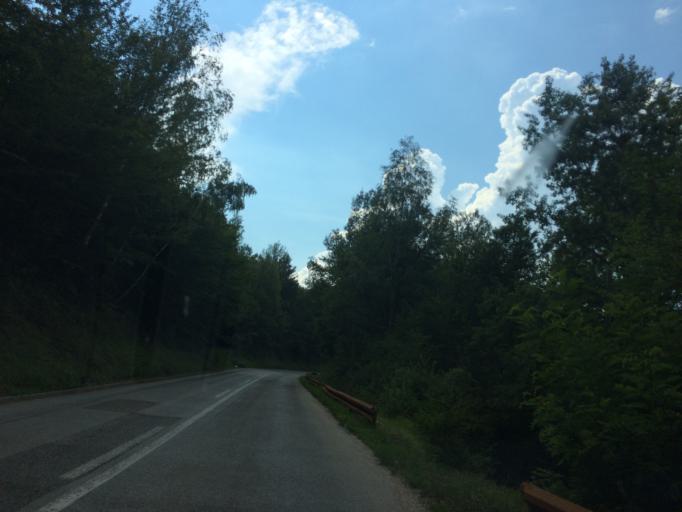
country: RS
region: Central Serbia
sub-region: Zlatiborski Okrug
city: Prijepolje
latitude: 43.3615
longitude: 19.6113
